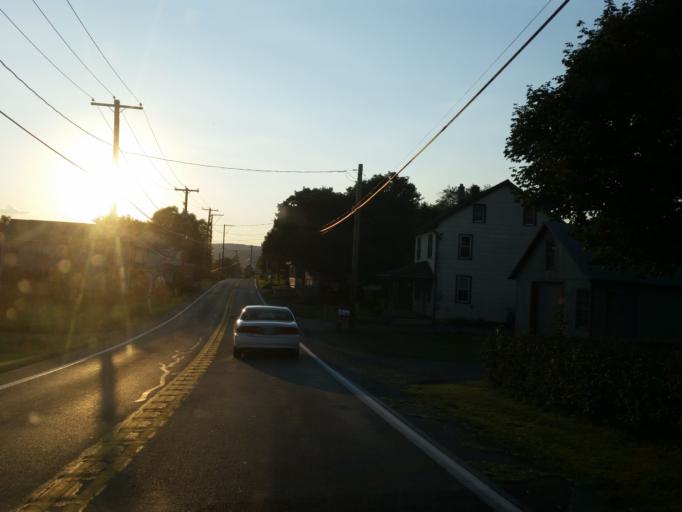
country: US
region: Pennsylvania
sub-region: Lancaster County
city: Reinholds
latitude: 40.2793
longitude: -76.1389
